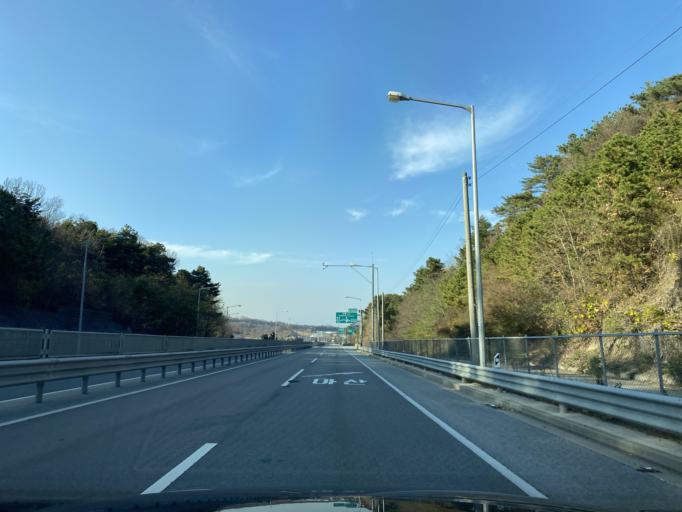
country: KR
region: Chungcheongnam-do
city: Asan
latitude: 36.7760
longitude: 126.9420
